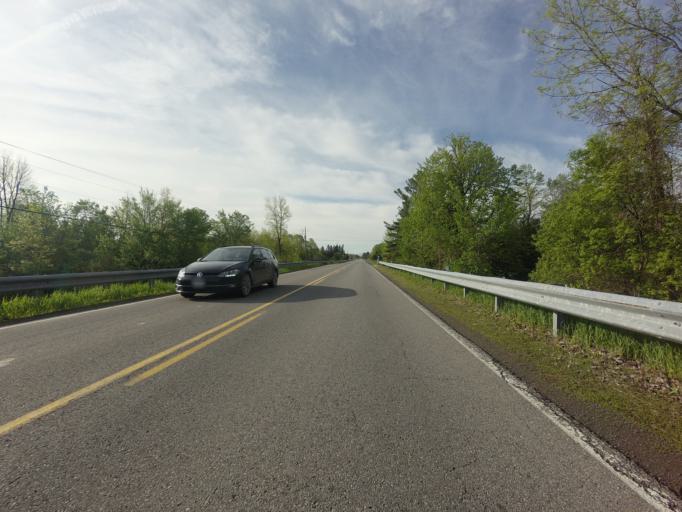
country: CA
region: Ontario
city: Ottawa
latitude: 45.2811
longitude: -75.4435
